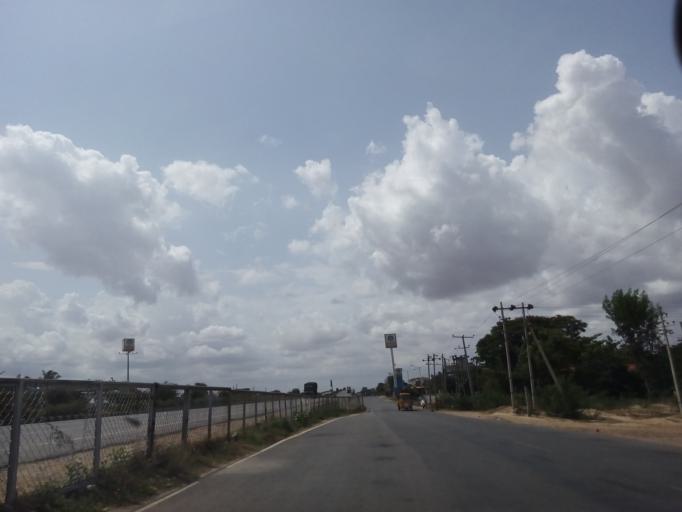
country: IN
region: Karnataka
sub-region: Tumkur
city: Sira
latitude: 13.7047
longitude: 76.9147
